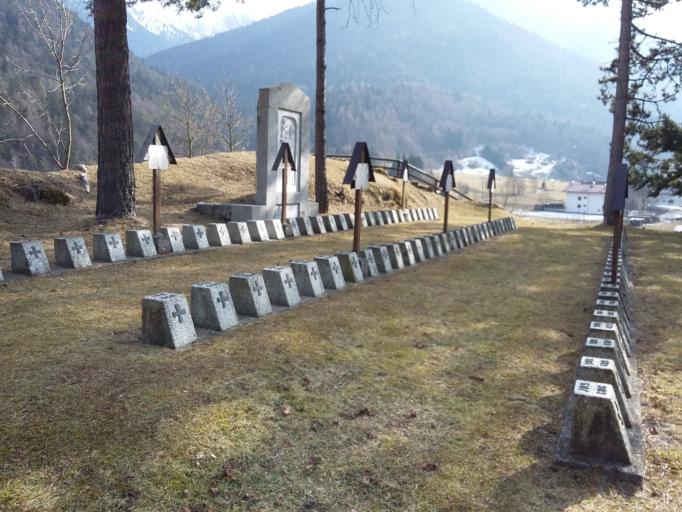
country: IT
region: Trentino-Alto Adige
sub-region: Provincia di Trento
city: Bondo
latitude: 46.0009
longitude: 10.6941
